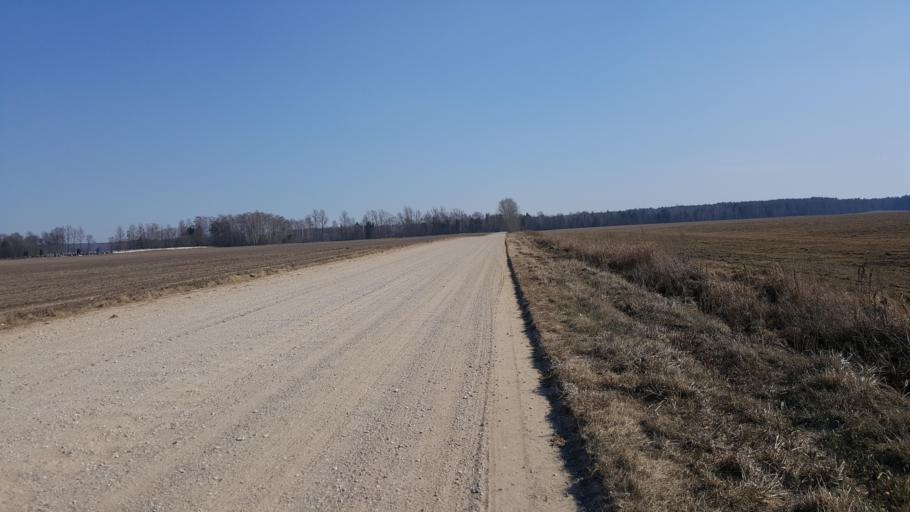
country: BY
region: Brest
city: Kamyanyets
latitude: 52.3575
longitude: 23.7674
